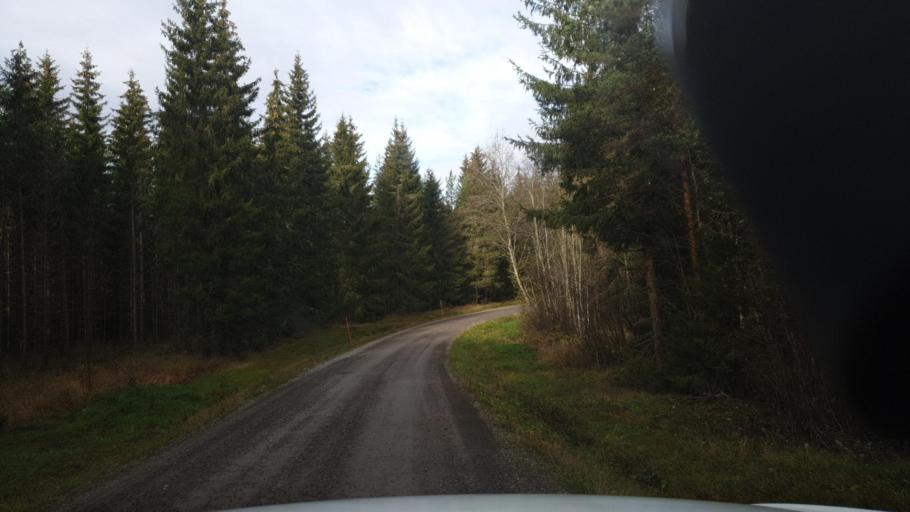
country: SE
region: Vaermland
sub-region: Eda Kommun
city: Charlottenberg
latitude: 59.9013
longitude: 12.3802
